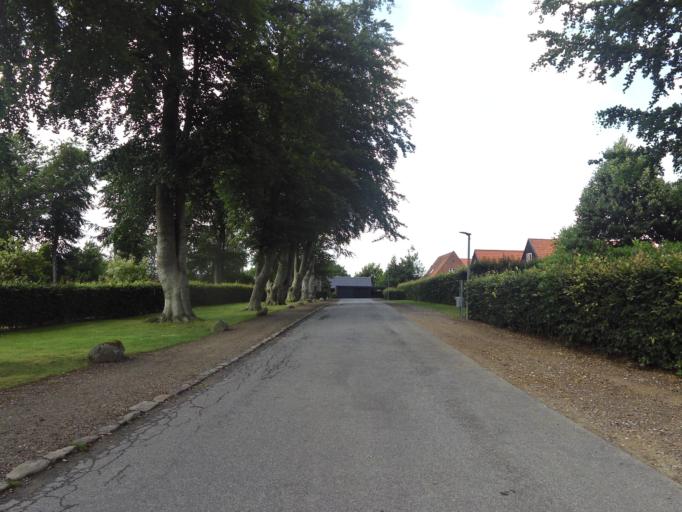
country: DK
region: South Denmark
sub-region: Vejen Kommune
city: Rodding
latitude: 55.3698
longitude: 9.0548
